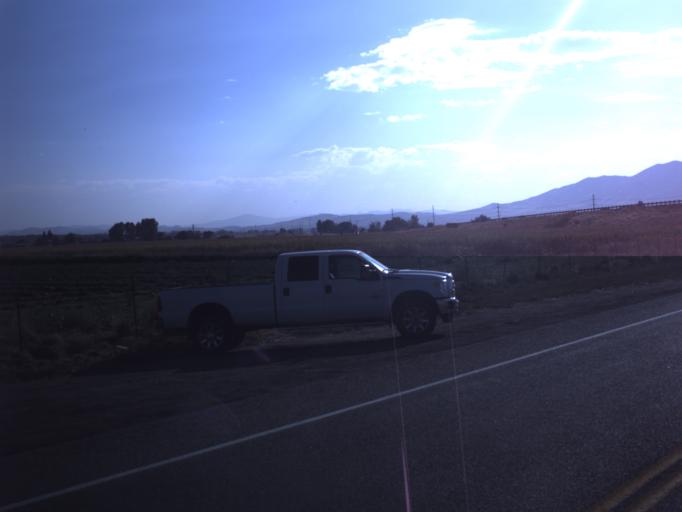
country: US
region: Utah
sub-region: Utah County
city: Benjamin
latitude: 40.0854
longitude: -111.6998
